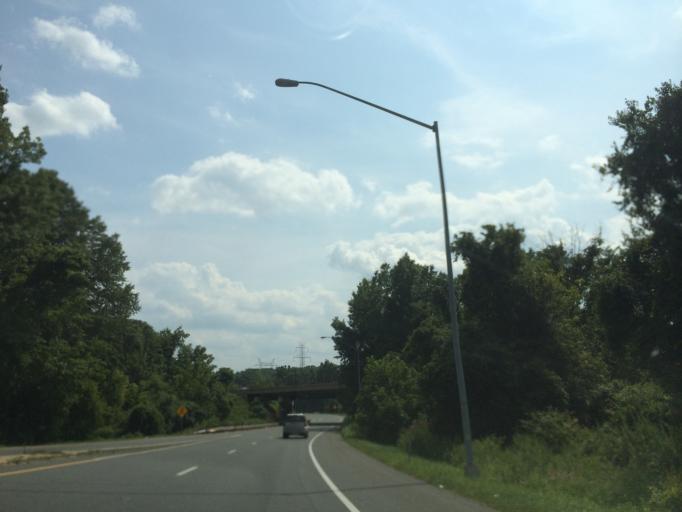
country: US
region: Maryland
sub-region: Howard County
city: Ellicott City
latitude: 39.2751
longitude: -76.8178
